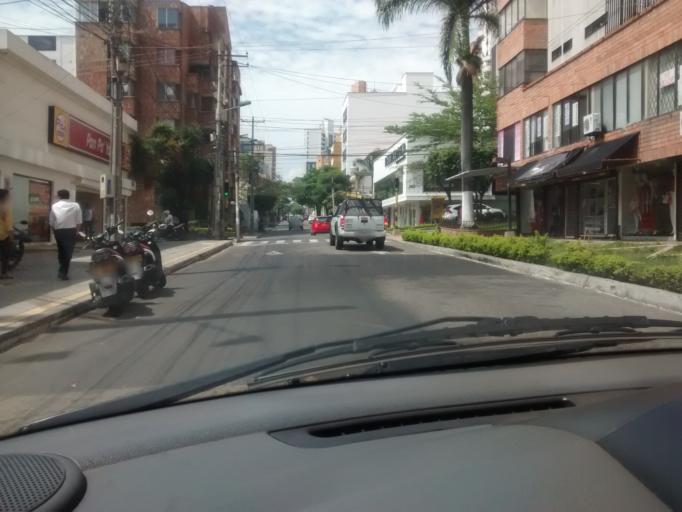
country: CO
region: Santander
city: Bucaramanga
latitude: 7.1167
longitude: -73.1086
